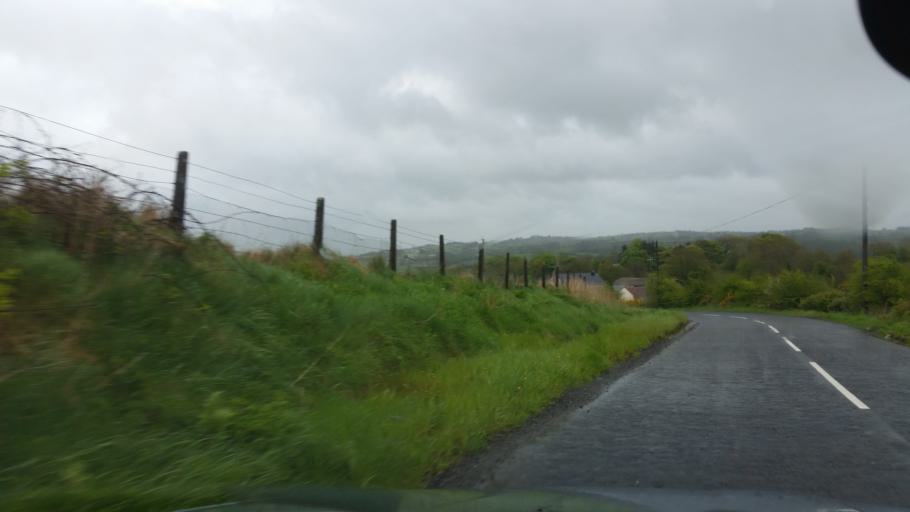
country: GB
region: Northern Ireland
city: Fintona
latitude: 54.4692
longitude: -7.3211
